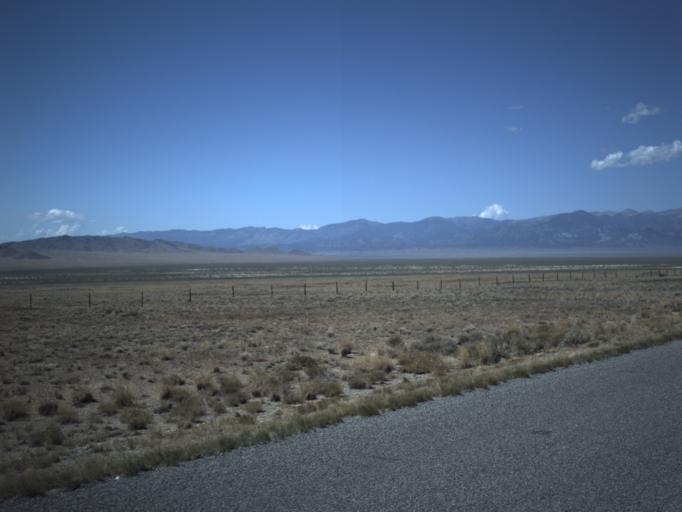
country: US
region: Nevada
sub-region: White Pine County
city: McGill
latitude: 39.0402
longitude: -113.8287
